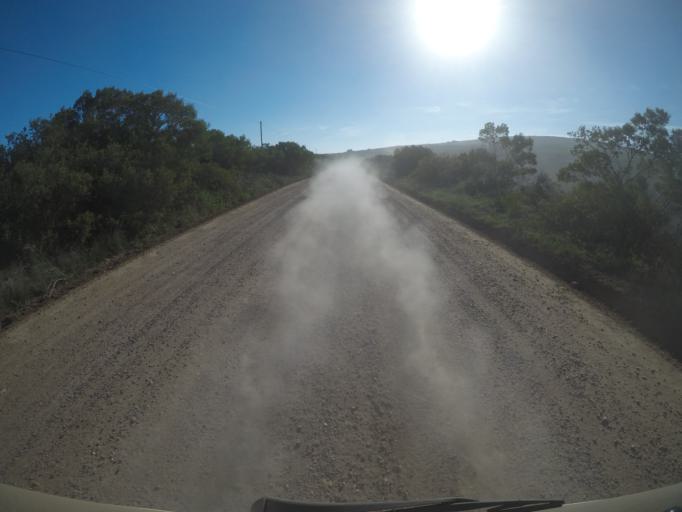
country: ZA
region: Western Cape
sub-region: Eden District Municipality
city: Mossel Bay
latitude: -34.1447
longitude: 22.0123
